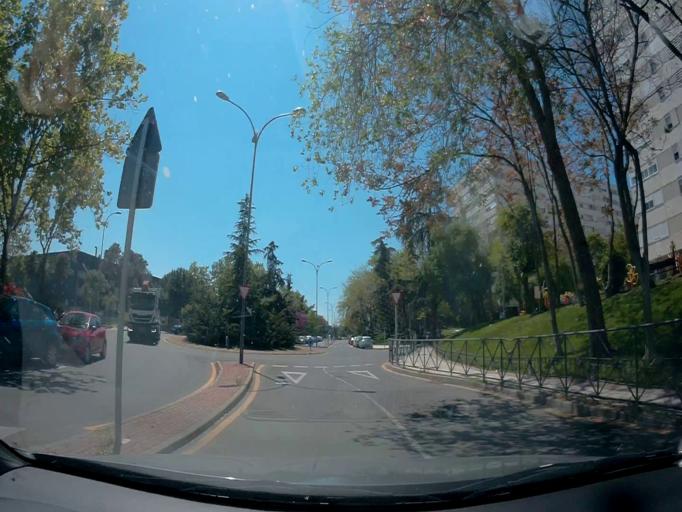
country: ES
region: Madrid
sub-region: Provincia de Madrid
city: Alcorcon
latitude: 40.3428
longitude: -3.8147
